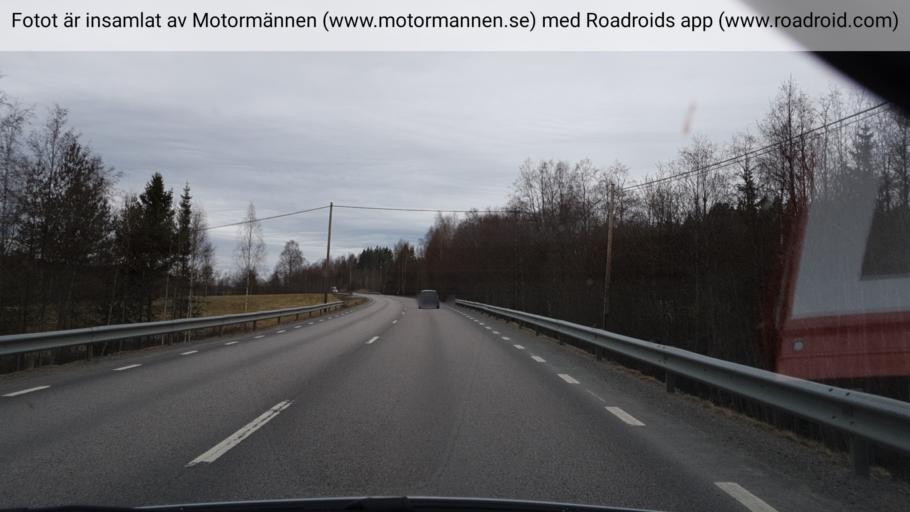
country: SE
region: Vaesternorrland
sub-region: Solleftea Kommun
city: Solleftea
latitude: 63.1907
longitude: 17.2431
